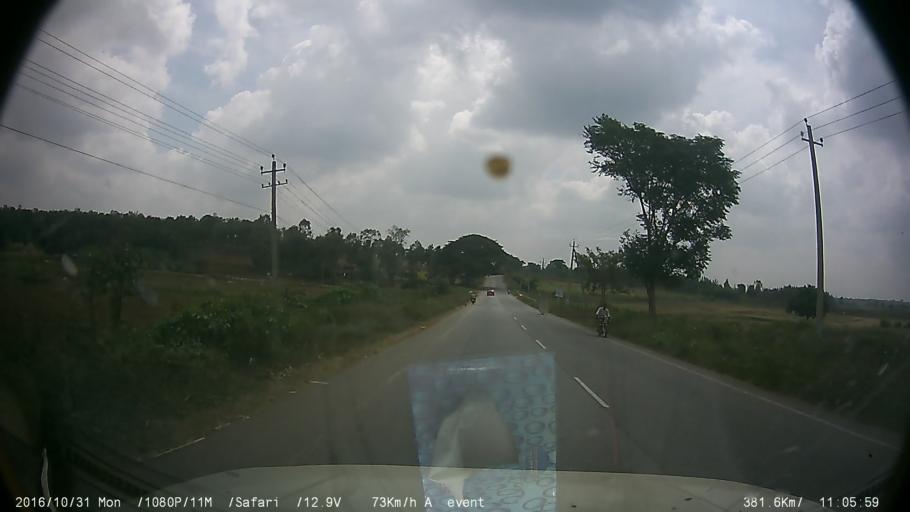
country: IN
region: Karnataka
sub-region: Mysore
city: Piriyapatna
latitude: 12.3772
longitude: 76.0383
